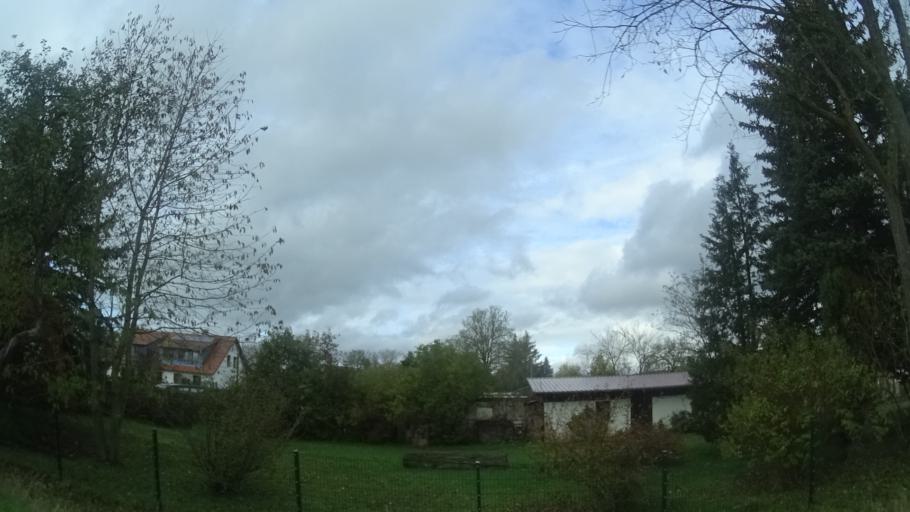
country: DE
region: Thuringia
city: Romhild
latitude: 50.4008
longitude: 10.5476
